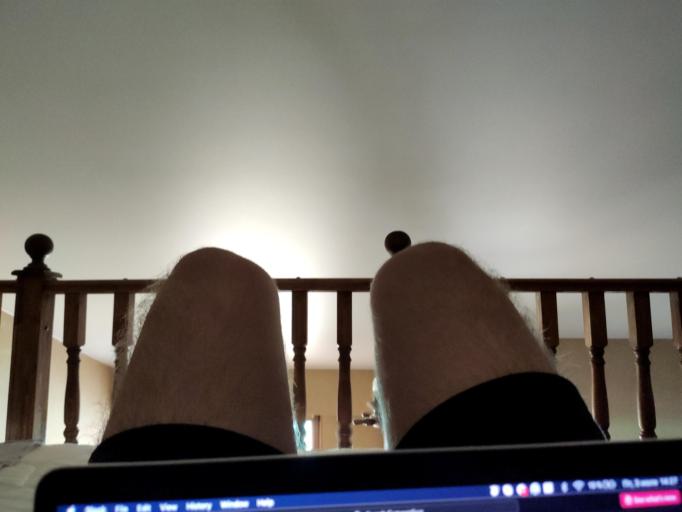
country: RU
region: Krasnodarskiy
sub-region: Sochi City
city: Khosta
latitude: 43.5452
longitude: 39.8036
